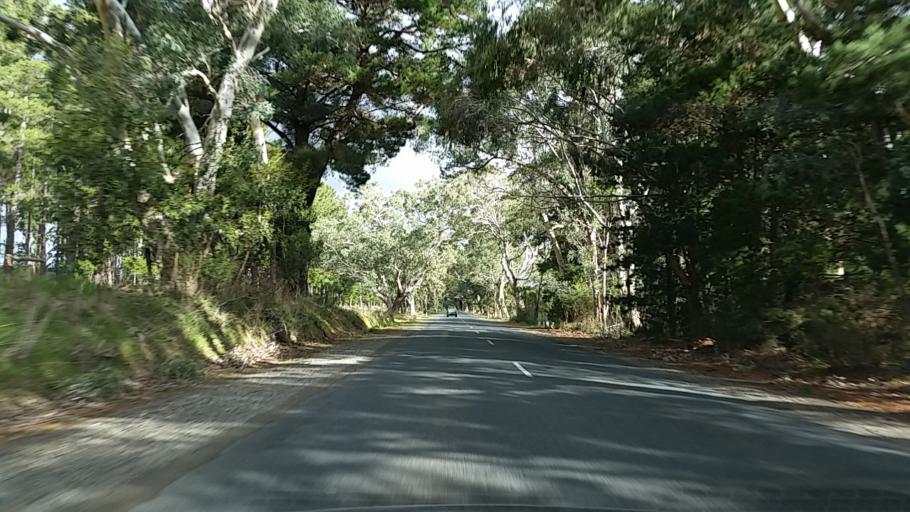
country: AU
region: South Australia
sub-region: Alexandrina
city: Mount Compass
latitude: -35.2554
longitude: 138.6619
